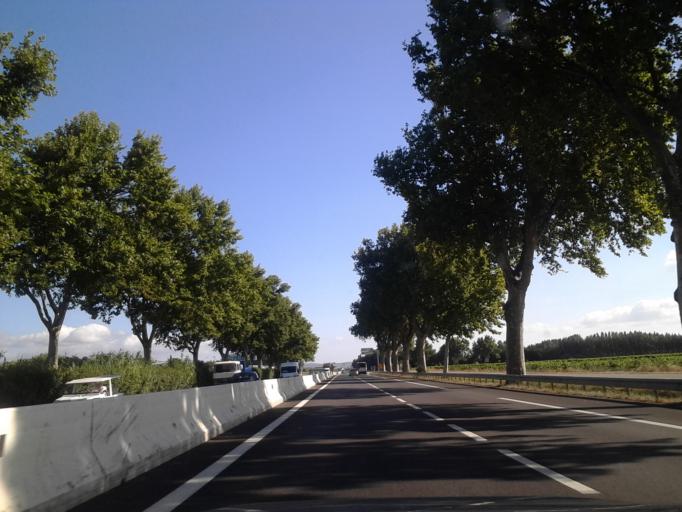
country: FR
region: Languedoc-Roussillon
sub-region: Departement des Pyrenees-Orientales
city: Rivesaltes
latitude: 42.7649
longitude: 2.8990
